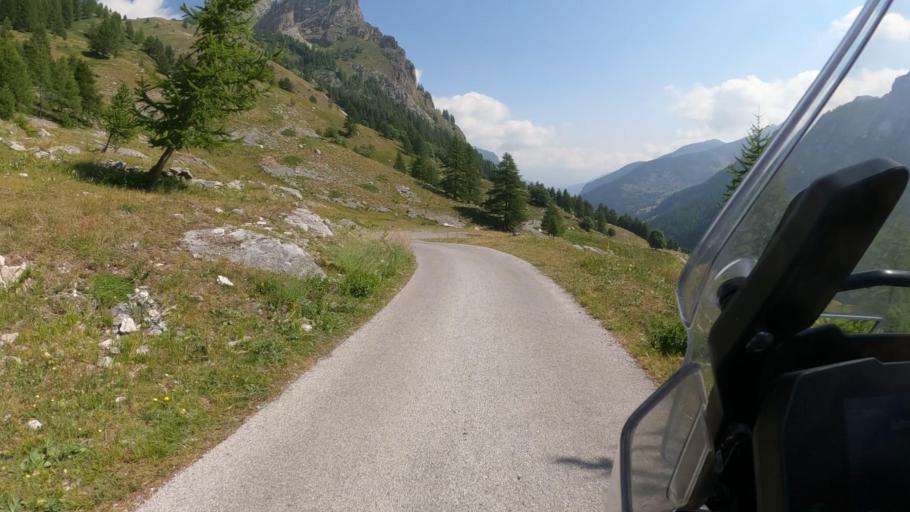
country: IT
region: Piedmont
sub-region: Provincia di Cuneo
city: Canosio
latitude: 44.4110
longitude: 7.0372
